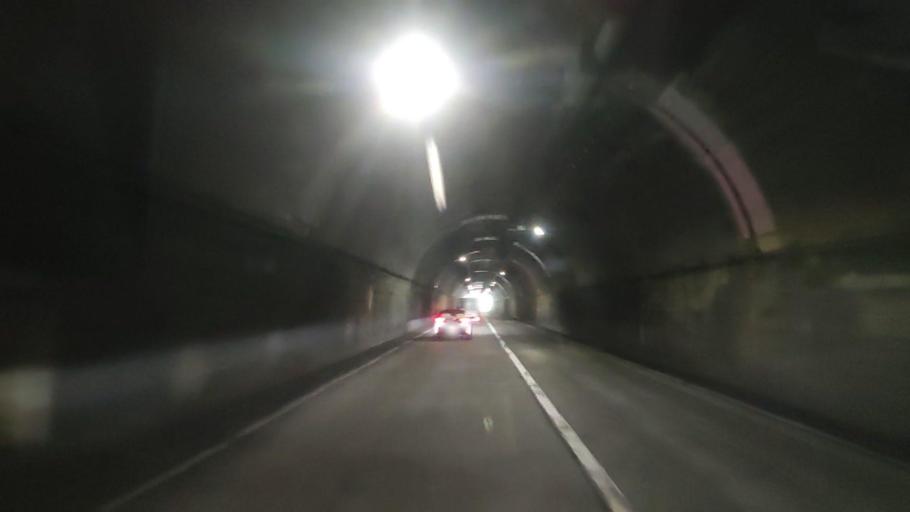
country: JP
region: Mie
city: Owase
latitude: 34.1556
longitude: 136.2650
